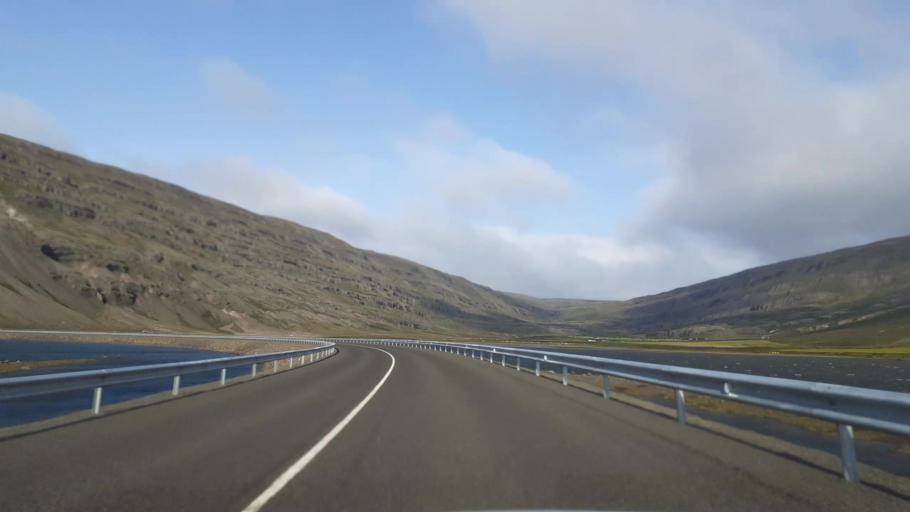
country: IS
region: East
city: Reydarfjoerdur
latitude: 64.7903
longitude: -14.4789
